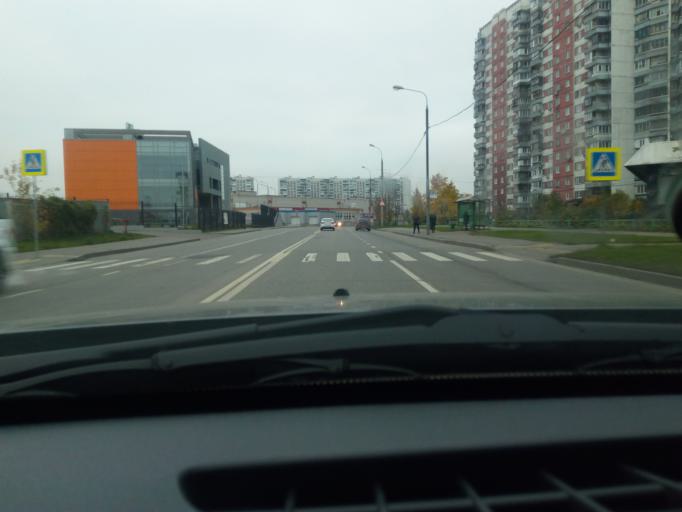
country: RU
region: Moskovskaya
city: Kuskovo
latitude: 55.7411
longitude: 37.8475
